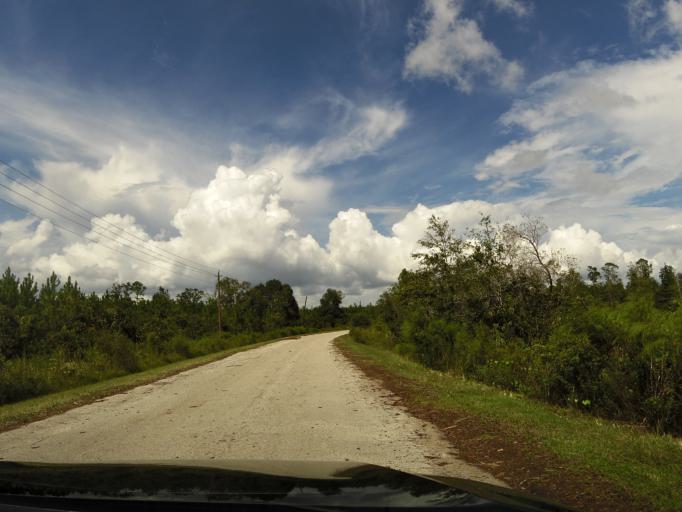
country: US
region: Florida
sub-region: Union County
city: Lake Butler
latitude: 30.0087
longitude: -82.3148
